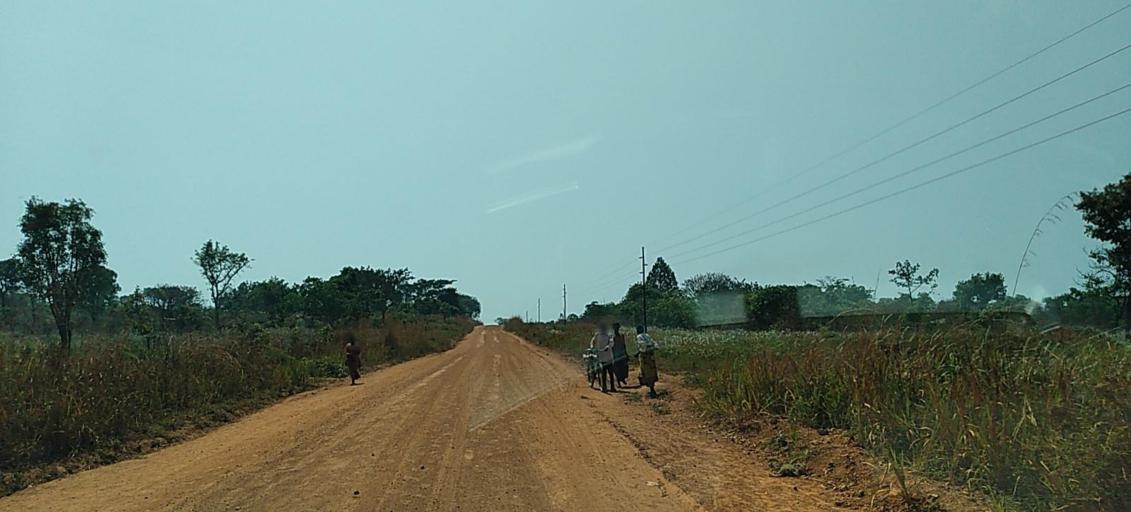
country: ZM
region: North-Western
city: Kansanshi
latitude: -12.0066
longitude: 26.5739
